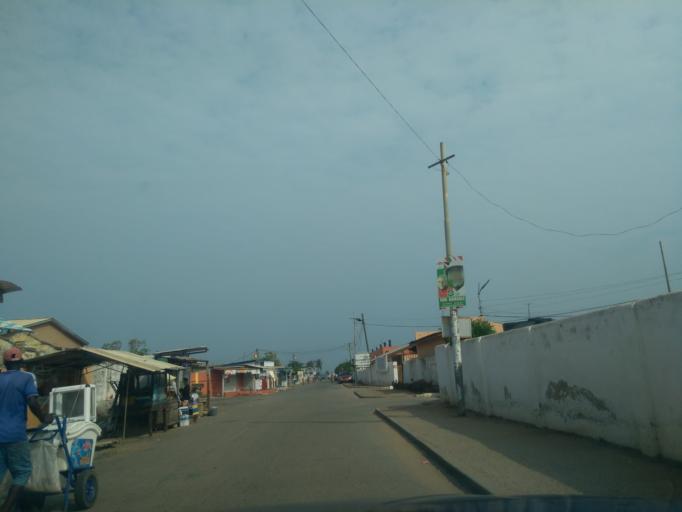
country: GH
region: Greater Accra
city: Accra
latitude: 5.5557
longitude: -0.1663
